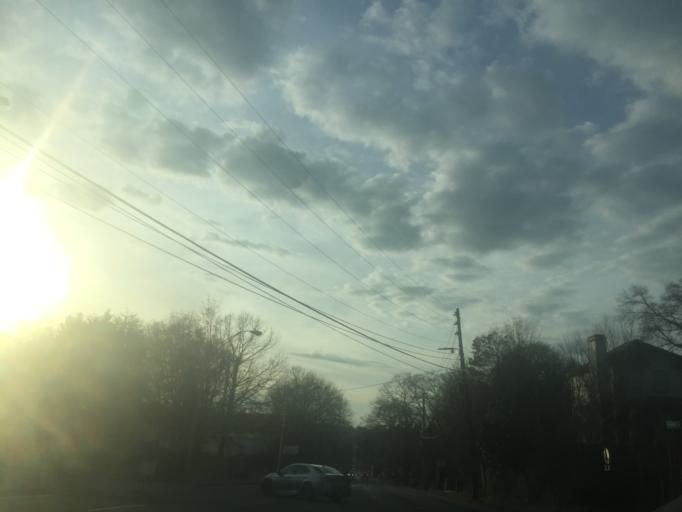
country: US
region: Georgia
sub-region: Fulton County
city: Atlanta
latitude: 33.7221
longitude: -84.3964
